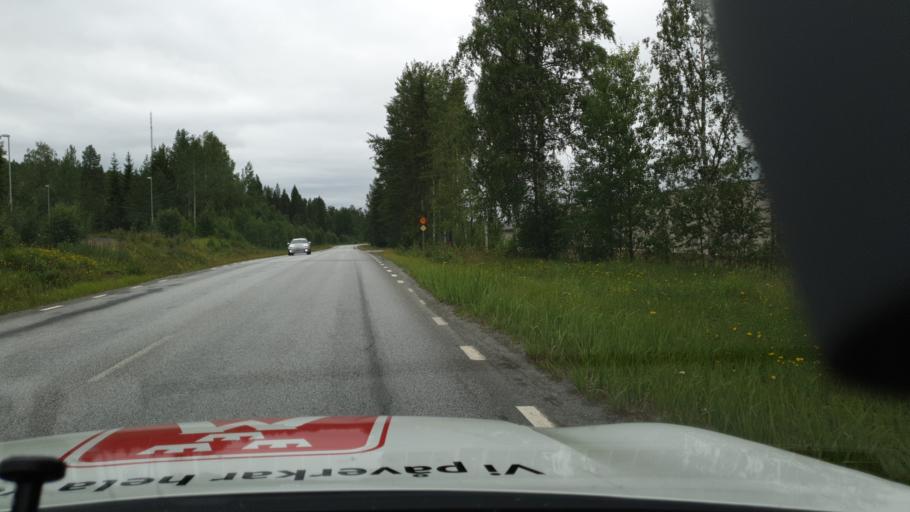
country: SE
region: Vaesterbotten
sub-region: Umea Kommun
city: Ersmark
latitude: 63.8638
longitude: 20.3006
